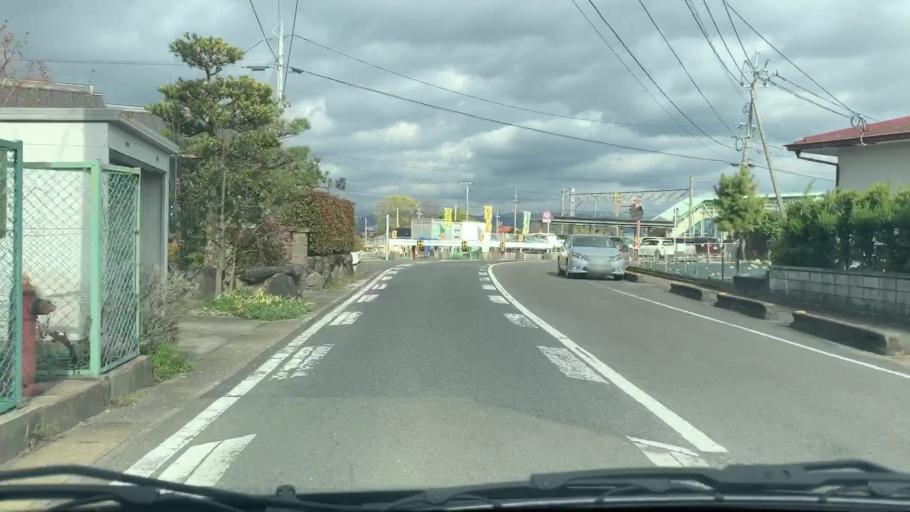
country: JP
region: Saga Prefecture
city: Saga-shi
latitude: 33.2549
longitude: 130.2282
